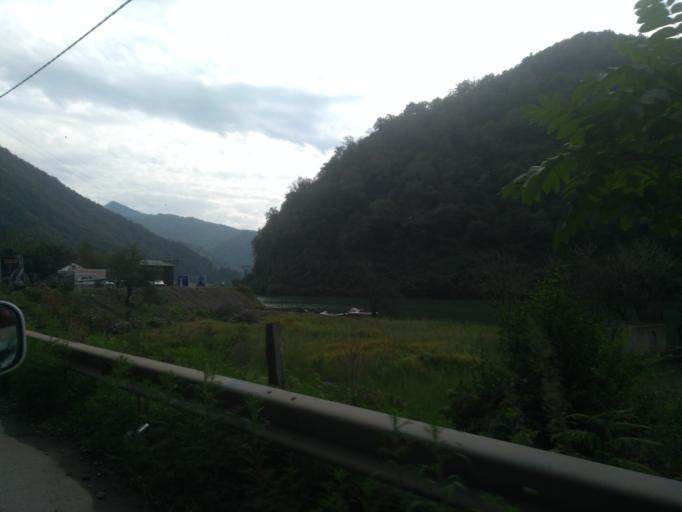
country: GE
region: Ajaria
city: Khelvachauri
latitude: 41.5445
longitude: 41.7149
